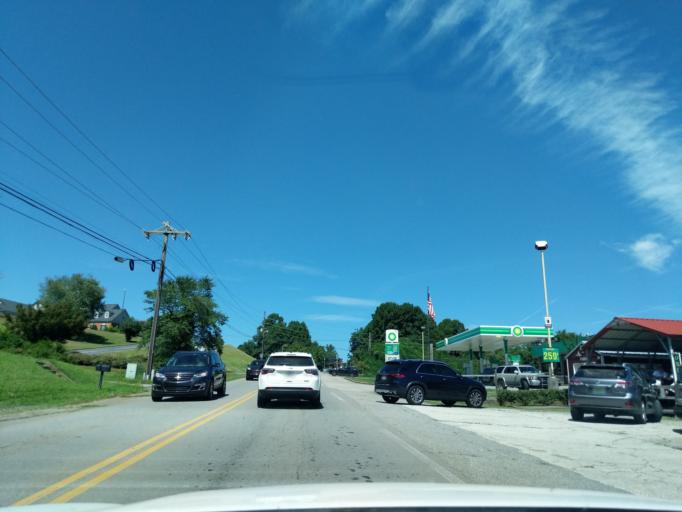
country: US
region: Georgia
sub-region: Fannin County
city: Blue Ridge
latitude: 34.8697
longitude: -84.3236
